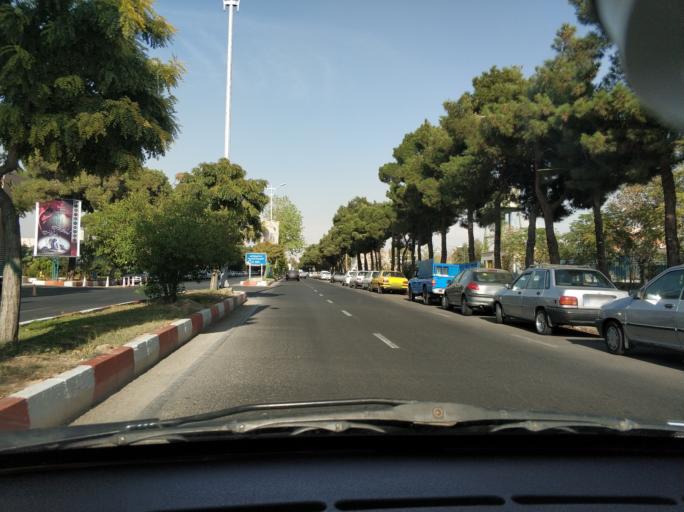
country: IR
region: Tehran
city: Tehran
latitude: 35.6964
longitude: 51.3300
